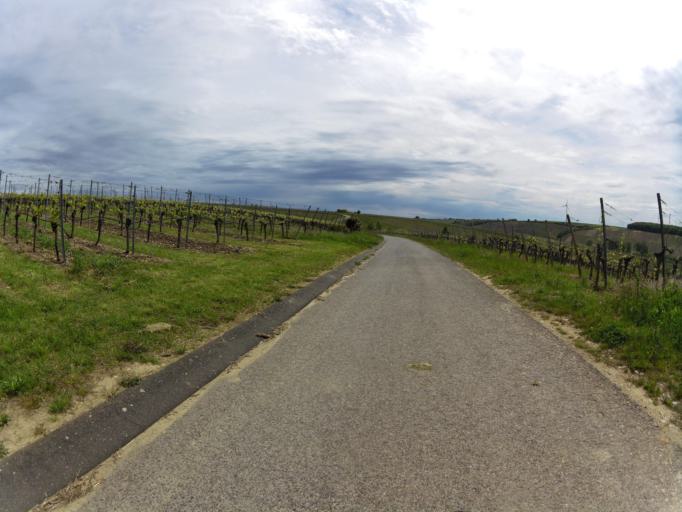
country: DE
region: Bavaria
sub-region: Regierungsbezirk Unterfranken
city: Nordheim
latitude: 49.8505
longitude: 10.1834
